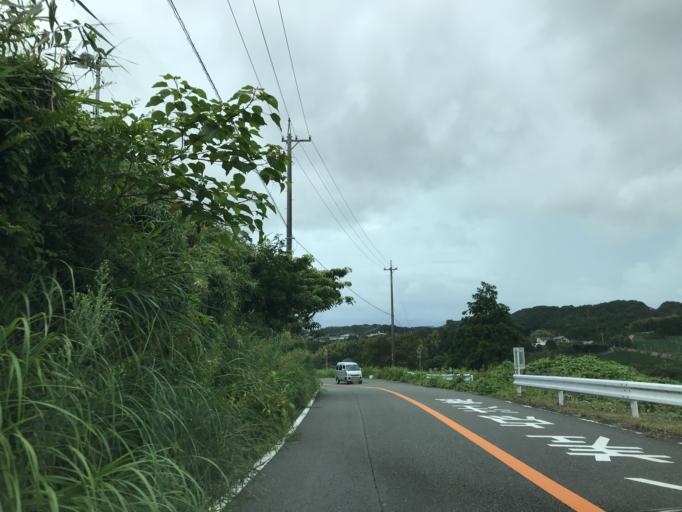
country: JP
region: Shizuoka
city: Sagara
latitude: 34.6750
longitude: 138.1435
